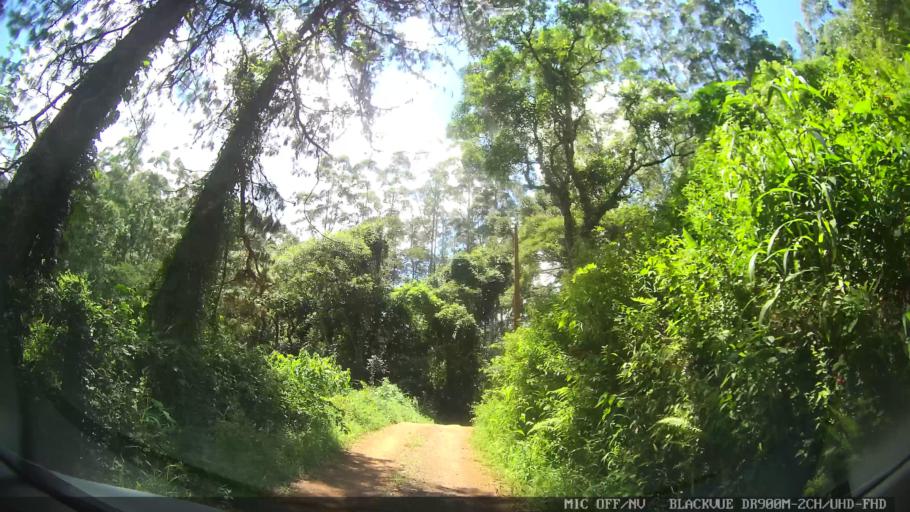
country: BR
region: Minas Gerais
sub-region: Extrema
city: Extrema
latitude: -22.8880
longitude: -46.2950
